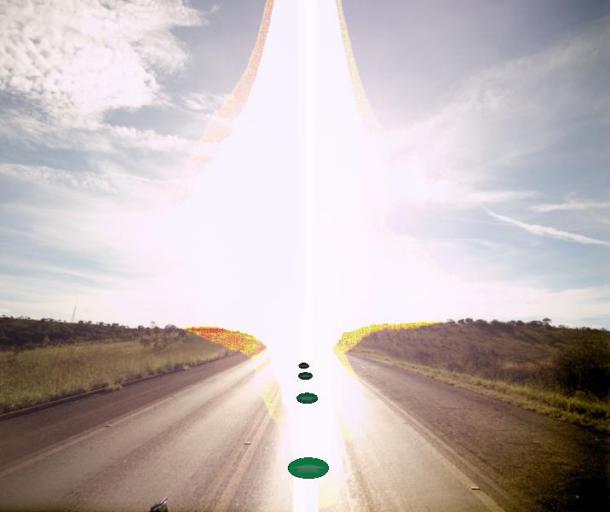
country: BR
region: Federal District
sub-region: Brasilia
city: Brasilia
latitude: -15.7536
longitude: -48.4157
